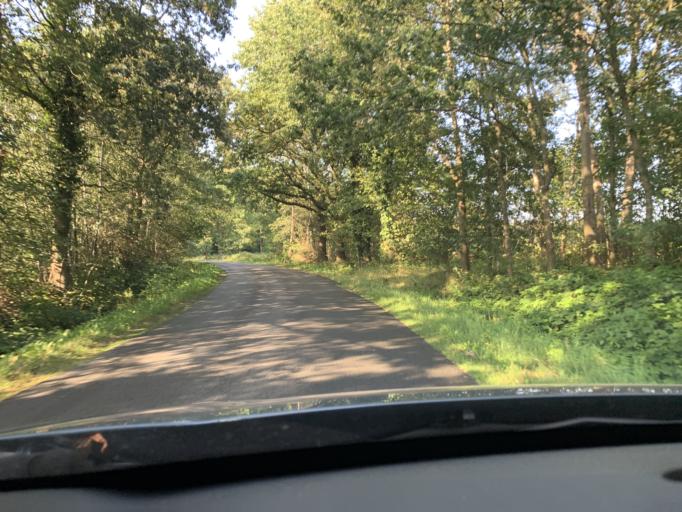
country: DE
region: Lower Saxony
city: Westerstede
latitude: 53.2601
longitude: 7.9082
